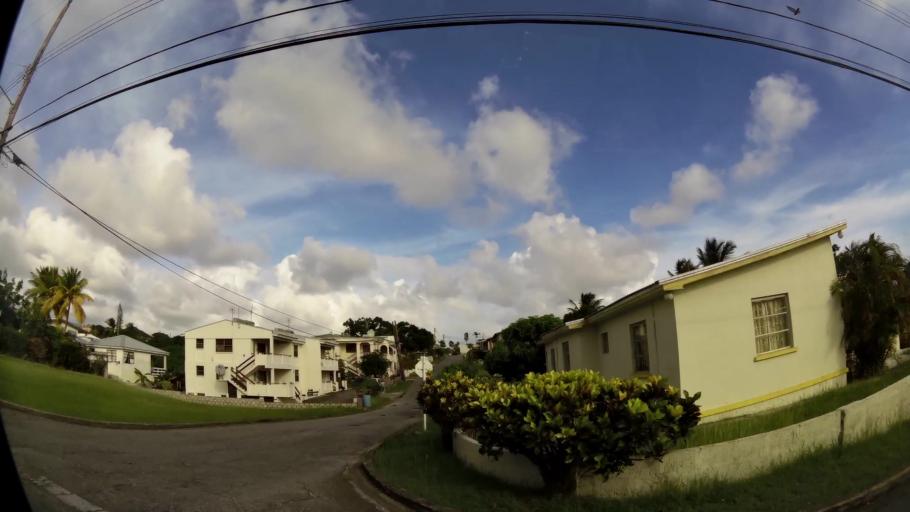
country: BB
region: Christ Church
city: Oistins
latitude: 13.0887
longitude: -59.5706
